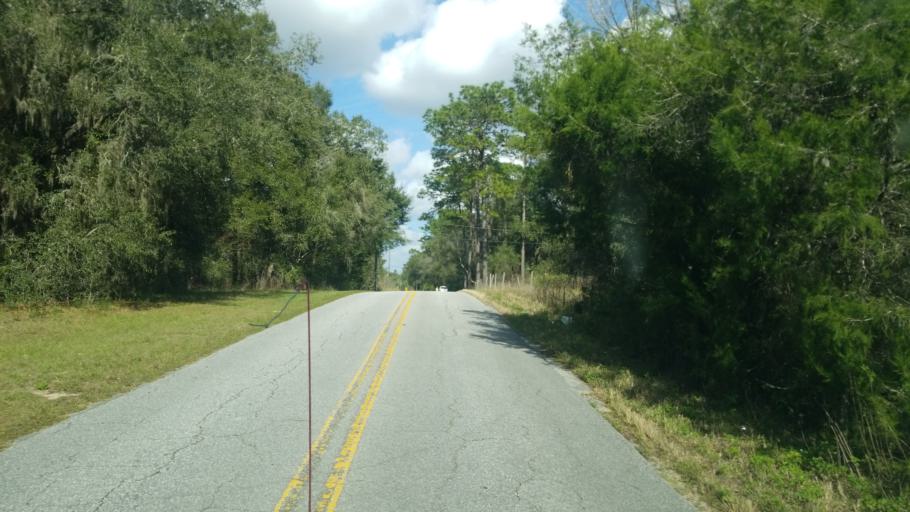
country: US
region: Florida
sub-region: Citrus County
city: Floral City
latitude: 28.7386
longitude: -82.2964
